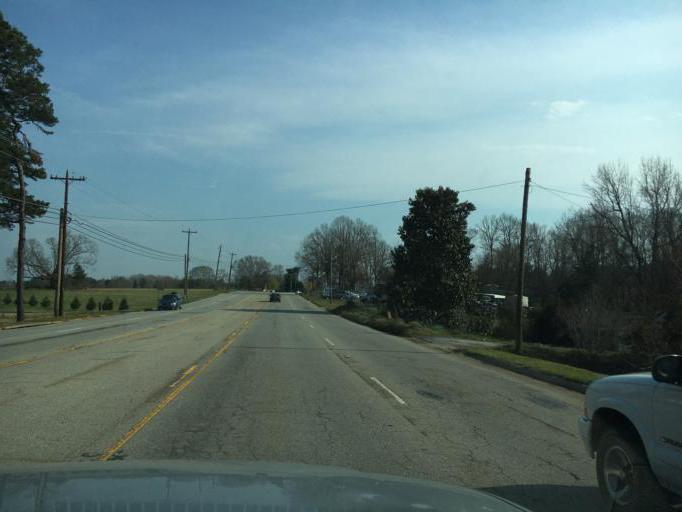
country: US
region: South Carolina
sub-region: Spartanburg County
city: Mayo
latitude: 35.1168
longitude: -81.8574
